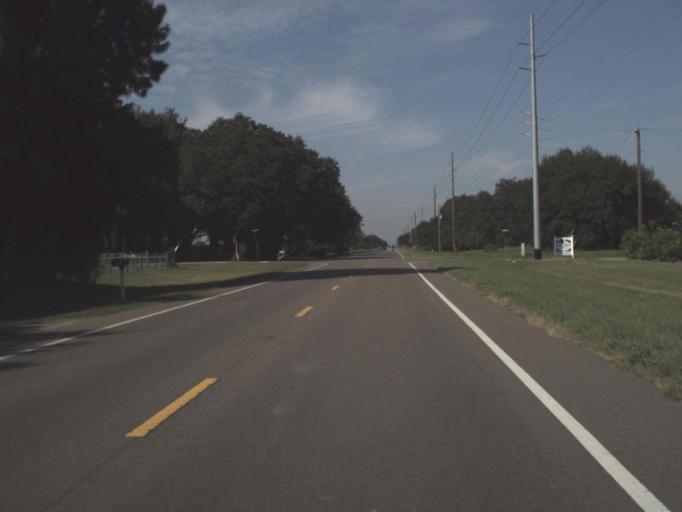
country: US
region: Florida
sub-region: Hardee County
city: Wauchula
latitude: 27.5515
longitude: -81.7020
